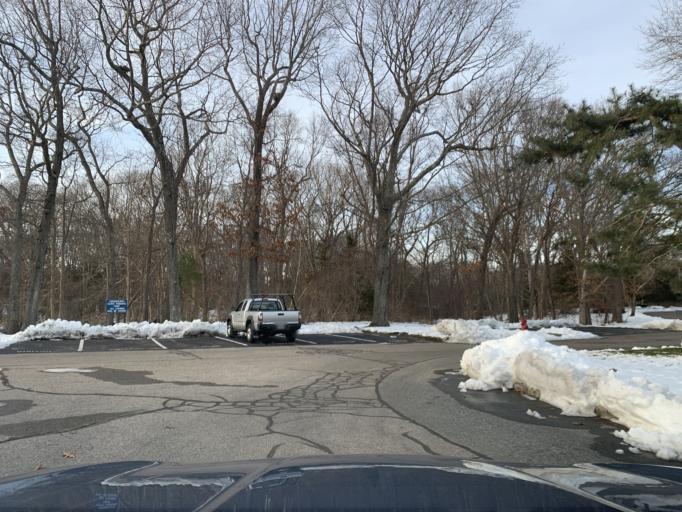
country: US
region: Rhode Island
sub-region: Washington County
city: North Kingstown
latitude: 41.5860
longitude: -71.4425
